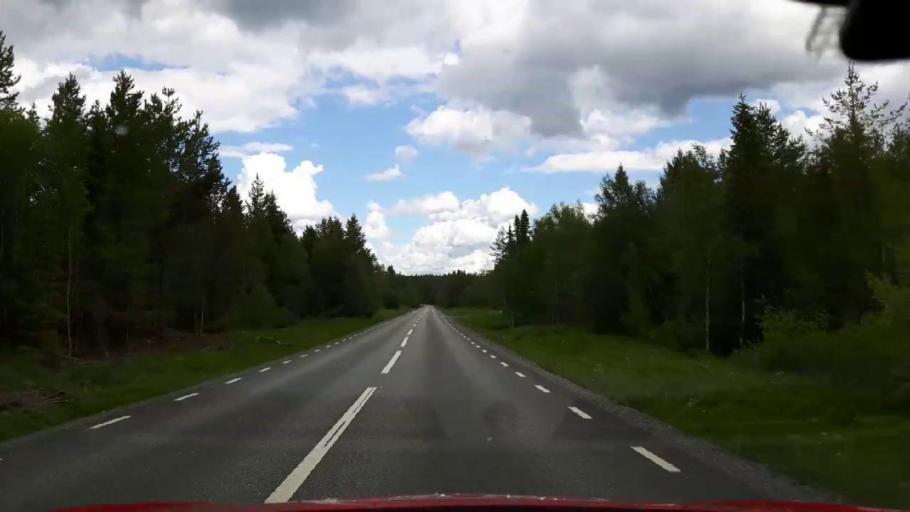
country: SE
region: Jaemtland
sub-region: Krokoms Kommun
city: Krokom
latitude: 63.7884
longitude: 14.3718
